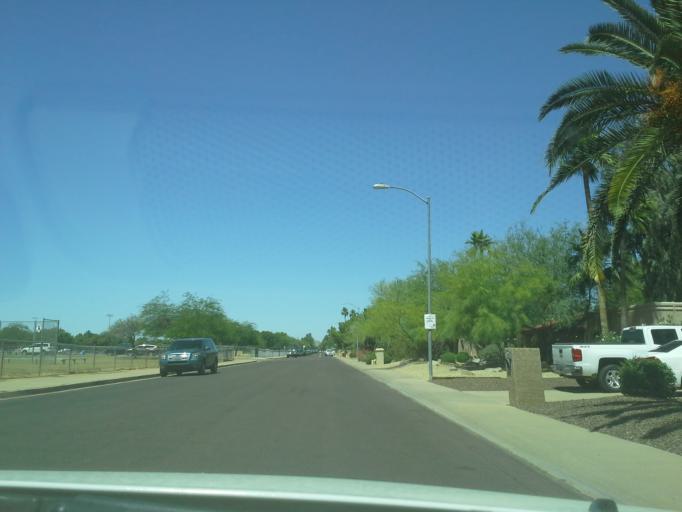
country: US
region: Arizona
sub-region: Maricopa County
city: Paradise Valley
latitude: 33.6079
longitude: -111.9532
